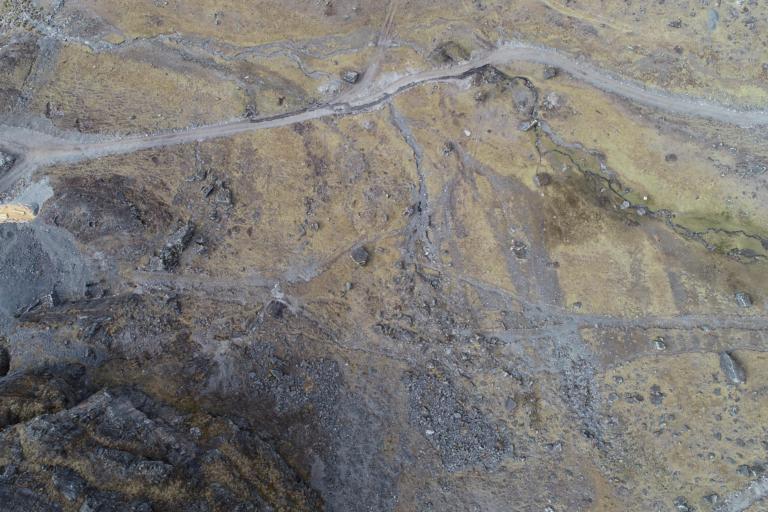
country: BO
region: La Paz
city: Sorata
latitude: -15.6696
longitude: -68.5523
